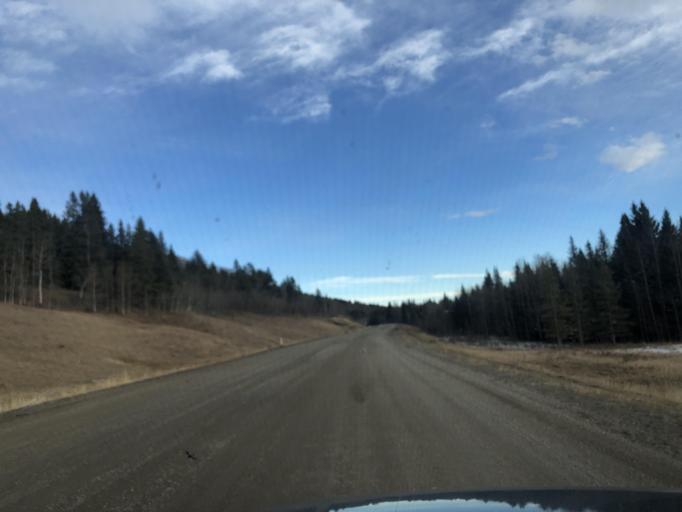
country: CA
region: Alberta
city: Cochrane
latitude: 51.0439
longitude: -114.7724
